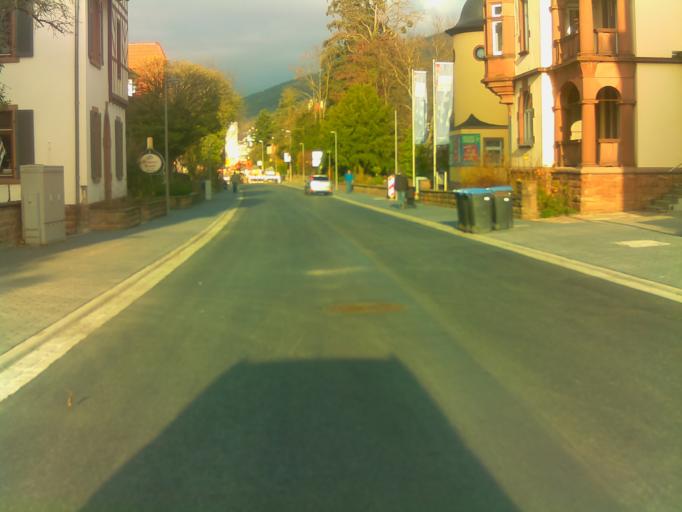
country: DE
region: Bavaria
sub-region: Regierungsbezirk Unterfranken
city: Miltenberg
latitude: 49.7043
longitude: 9.2620
